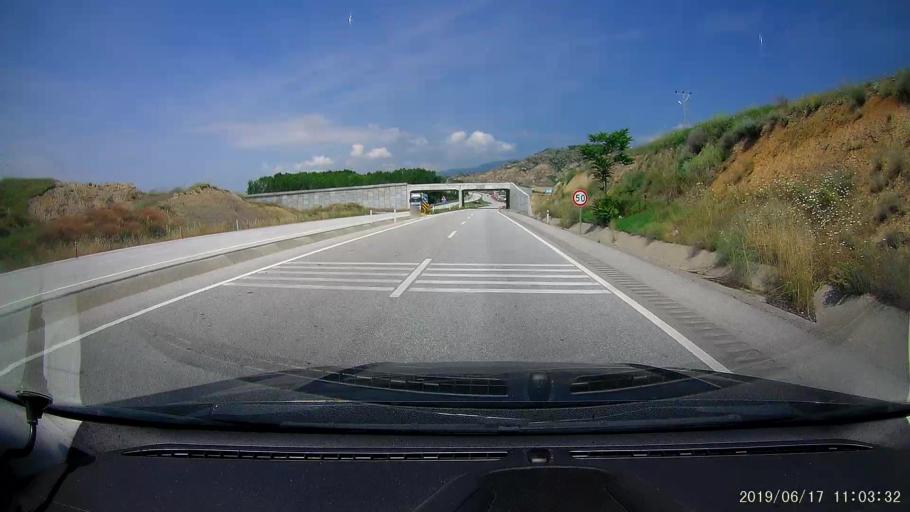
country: TR
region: Kastamonu
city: Tosya
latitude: 41.0180
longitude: 34.1141
